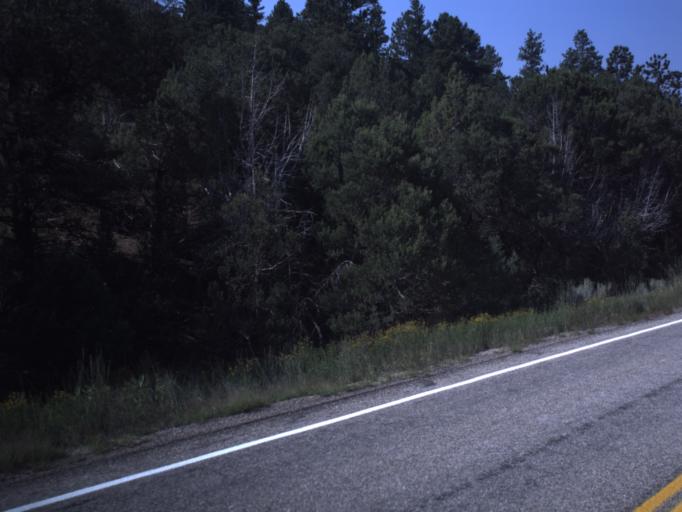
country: US
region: Utah
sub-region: Daggett County
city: Manila
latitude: 40.9117
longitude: -109.4311
